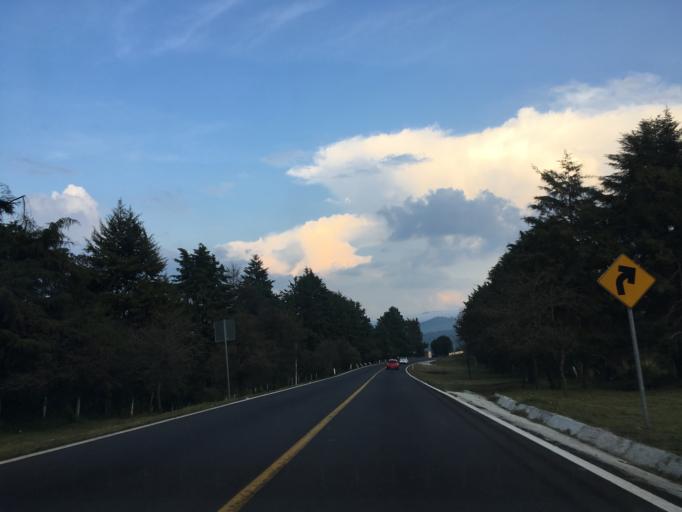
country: MX
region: Michoacan
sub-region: Patzcuaro
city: Santa Maria Huiramangaro (San Juan Tumbio)
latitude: 19.4925
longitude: -101.7460
